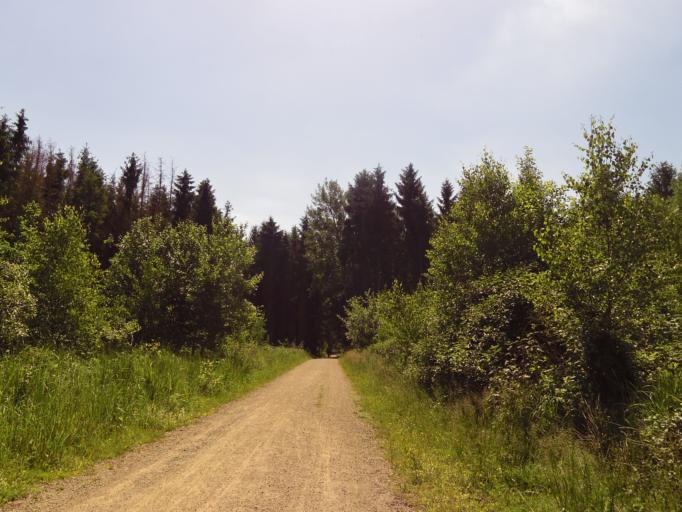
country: DE
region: Hesse
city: Langen
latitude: 50.0001
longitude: 8.6337
